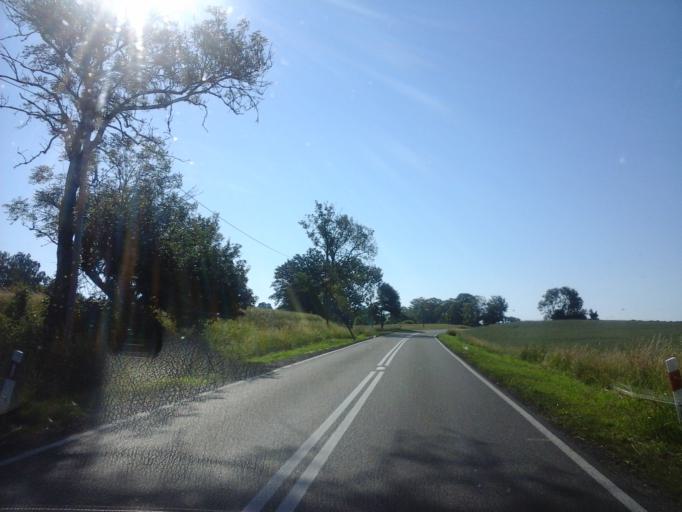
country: PL
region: West Pomeranian Voivodeship
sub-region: Powiat lobeski
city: Wegorzyno
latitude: 53.5052
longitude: 15.6565
